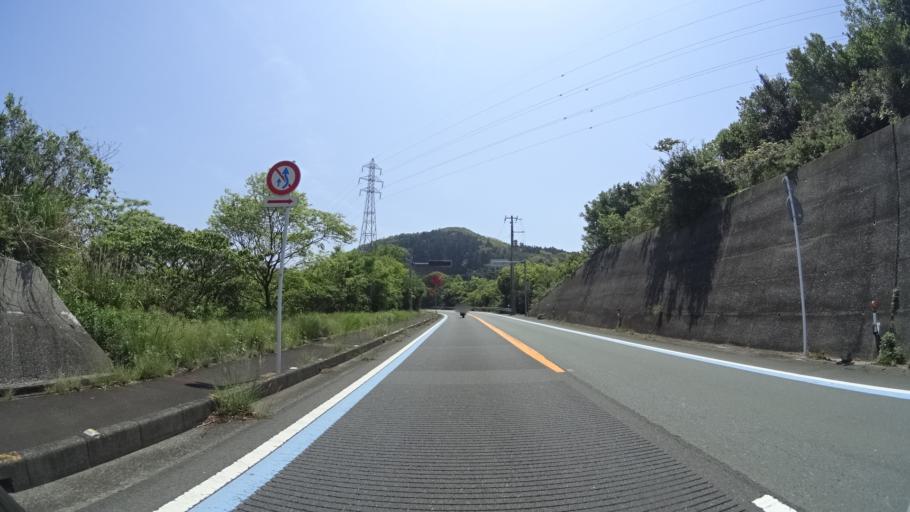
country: JP
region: Ehime
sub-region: Nishiuwa-gun
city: Ikata-cho
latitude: 33.4470
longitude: 132.2604
